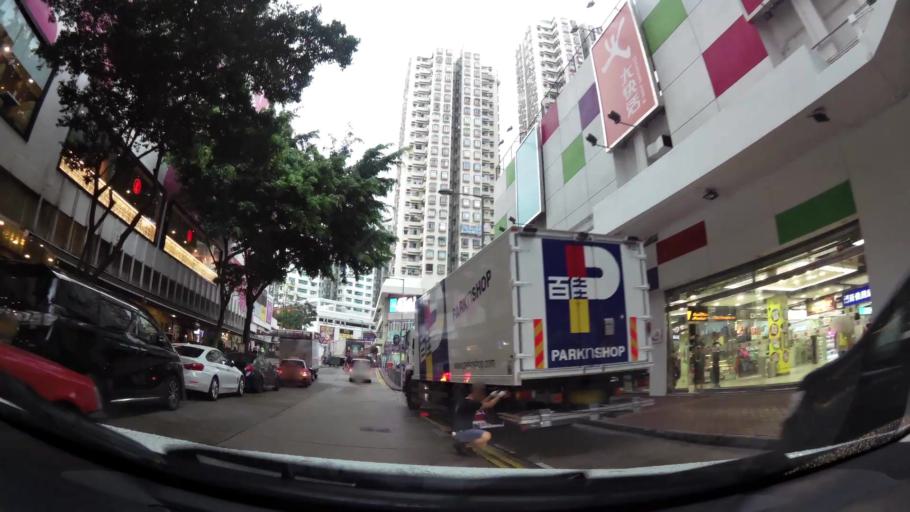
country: HK
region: Tsuen Wan
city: Tsuen Wan
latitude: 22.3688
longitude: 114.1211
